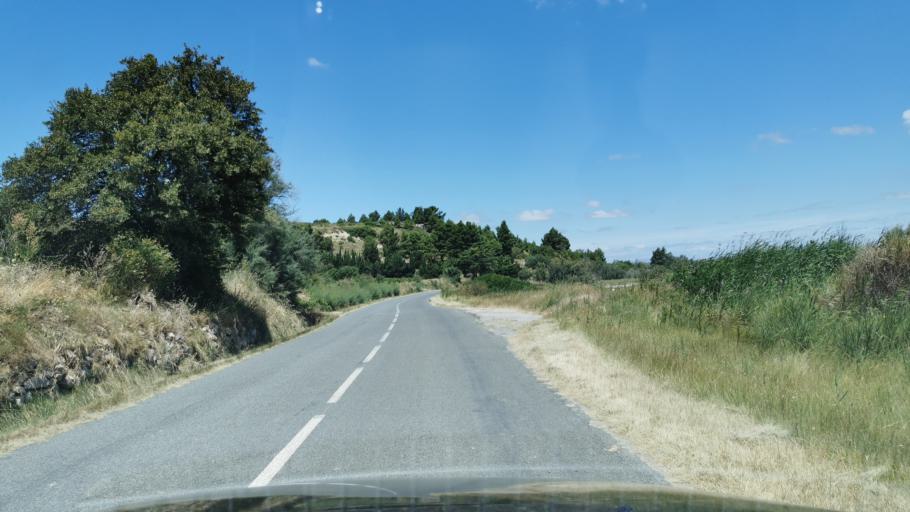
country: FR
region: Languedoc-Roussillon
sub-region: Departement de l'Aude
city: Peyriac-de-Mer
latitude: 43.1298
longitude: 2.9861
